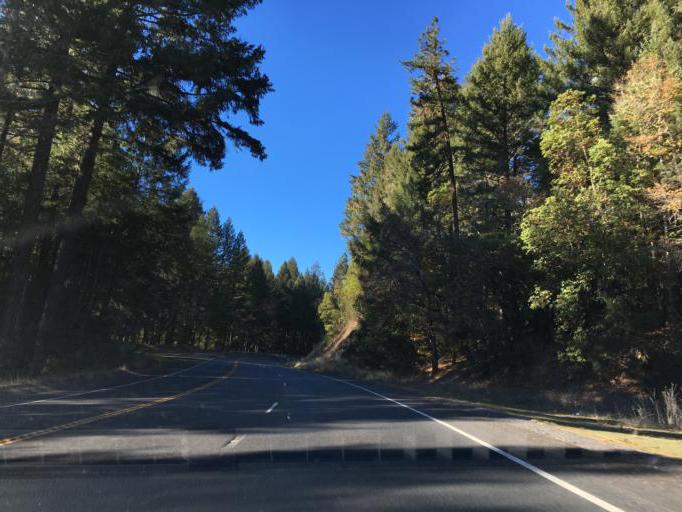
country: US
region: California
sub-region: Mendocino County
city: Brooktrails
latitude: 39.4656
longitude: -123.3519
